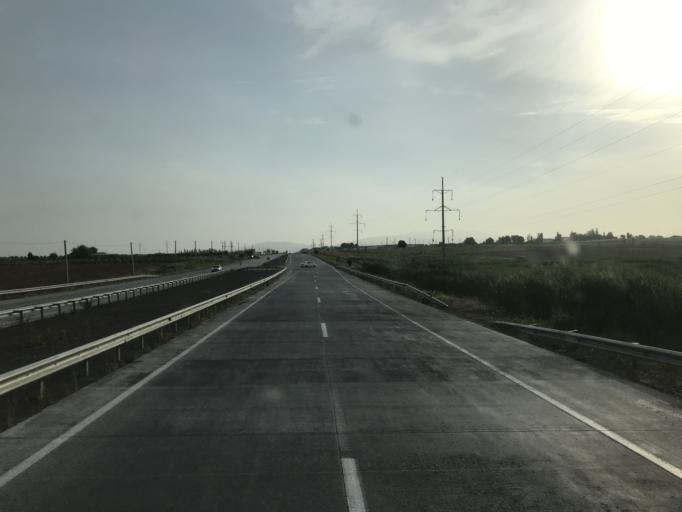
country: UZ
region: Toshkent
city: Qibray
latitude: 41.5218
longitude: 69.3947
